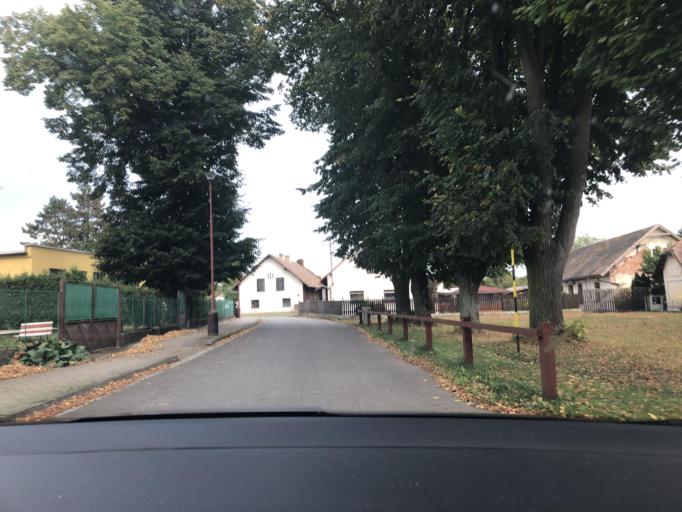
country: CZ
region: Pardubicky
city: Recany nad Labem
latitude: 50.0569
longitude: 15.4882
